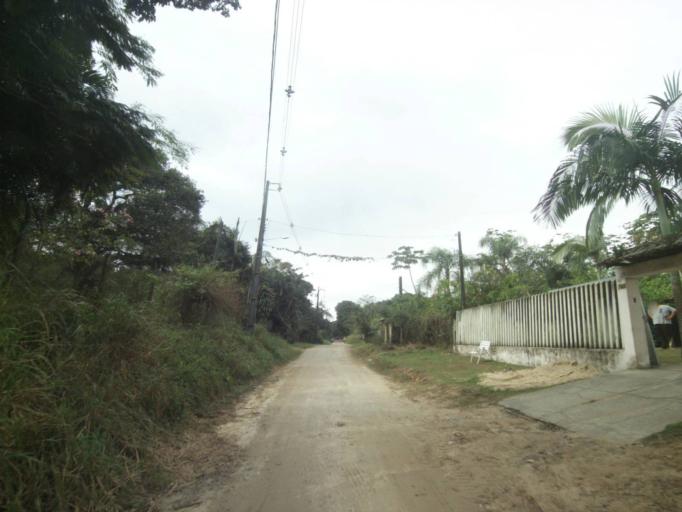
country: BR
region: Parana
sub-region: Paranagua
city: Paranagua
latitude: -25.5420
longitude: -48.5558
